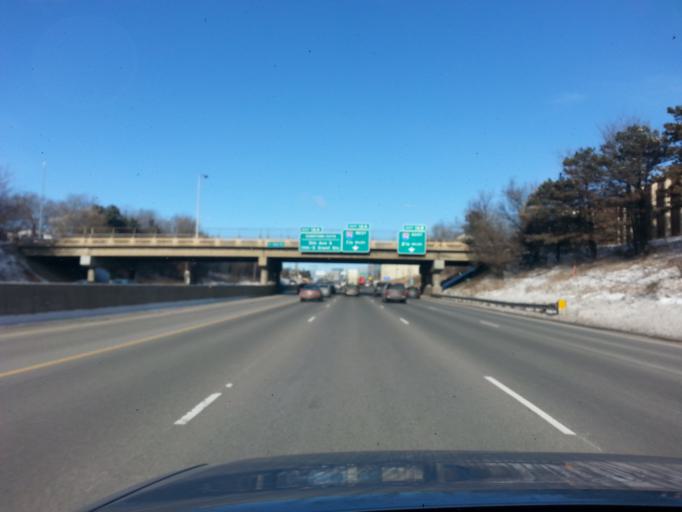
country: US
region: Minnesota
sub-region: Hennepin County
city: Minneapolis
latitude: 44.9389
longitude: -93.2746
